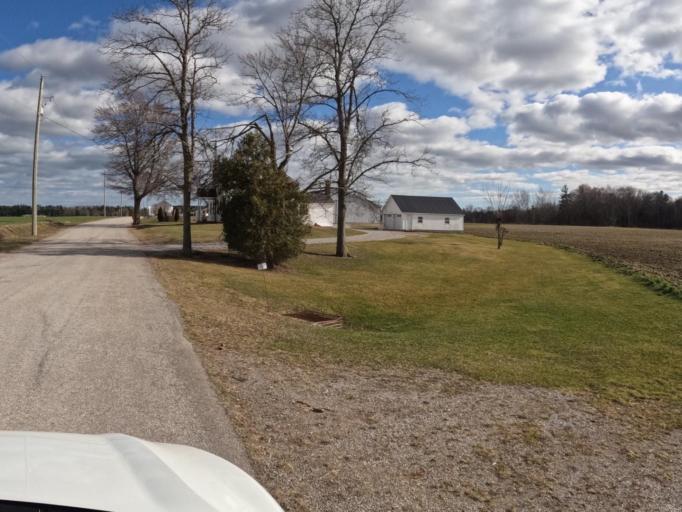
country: CA
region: Ontario
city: Norfolk County
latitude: 42.7498
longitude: -80.3857
